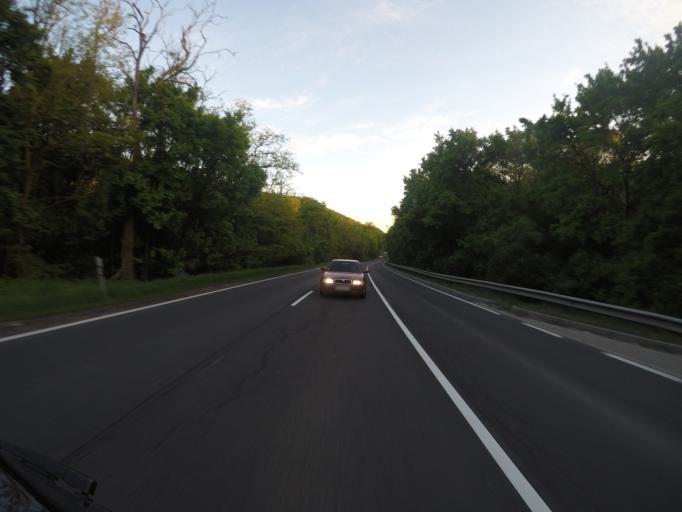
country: HU
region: Nograd
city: Retsag
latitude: 47.8665
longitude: 19.1091
